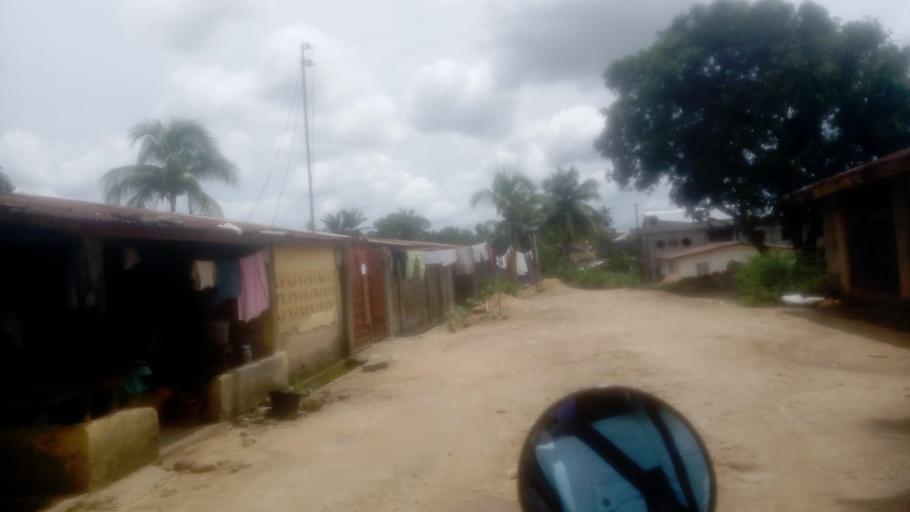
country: SL
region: Southern Province
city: Bo
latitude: 7.9528
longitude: -11.7160
